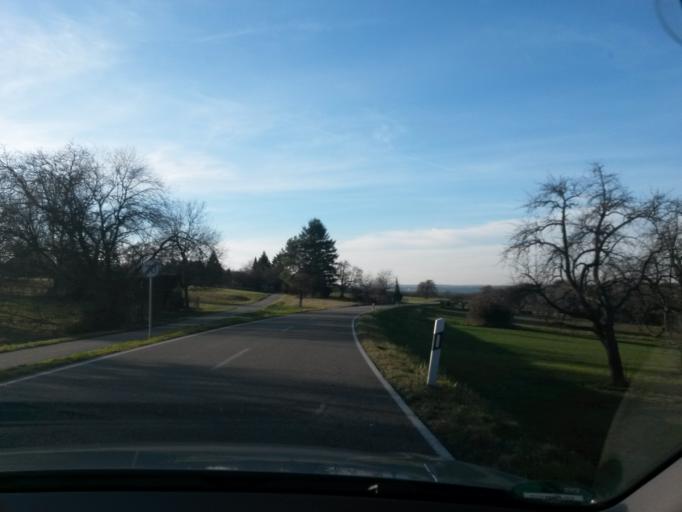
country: DE
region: Baden-Wuerttemberg
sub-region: Karlsruhe Region
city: Birkenfeld
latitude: 48.8707
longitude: 8.6170
